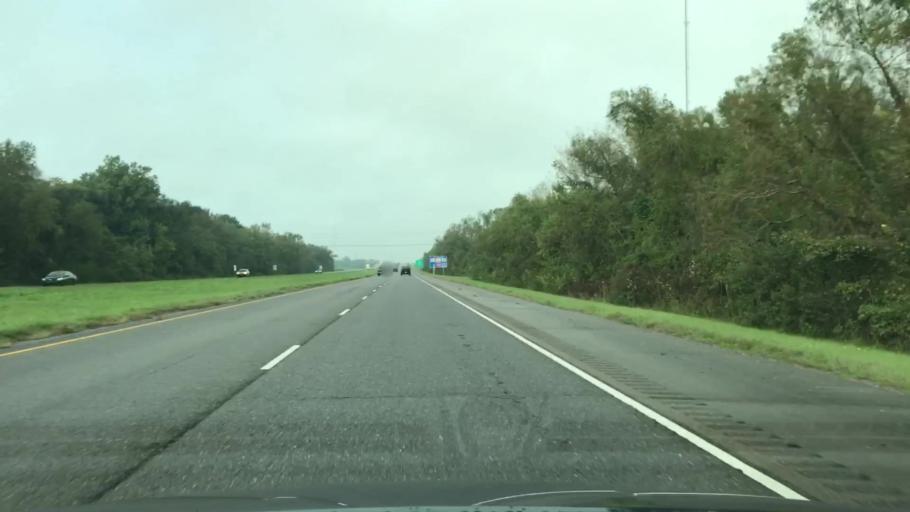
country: US
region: Louisiana
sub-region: Terrebonne Parish
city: Gray
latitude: 29.6809
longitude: -90.7714
